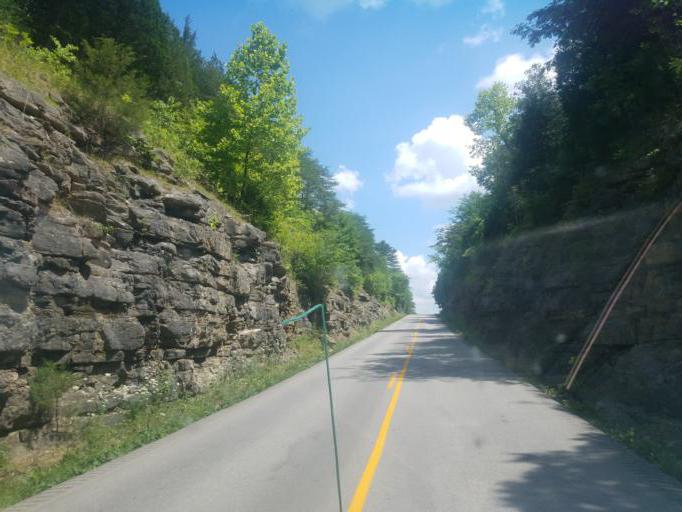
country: US
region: Kentucky
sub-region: Edmonson County
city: Brownsville
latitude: 37.3373
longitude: -86.1268
